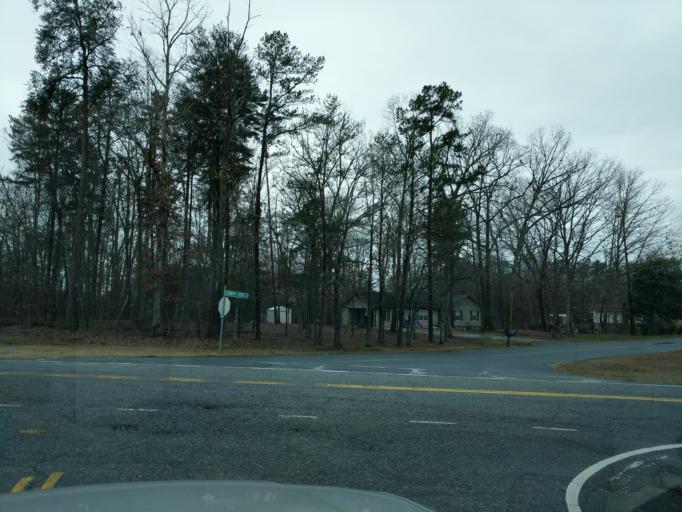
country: US
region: South Carolina
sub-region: Oconee County
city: Walhalla
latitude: 34.7895
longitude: -83.0814
